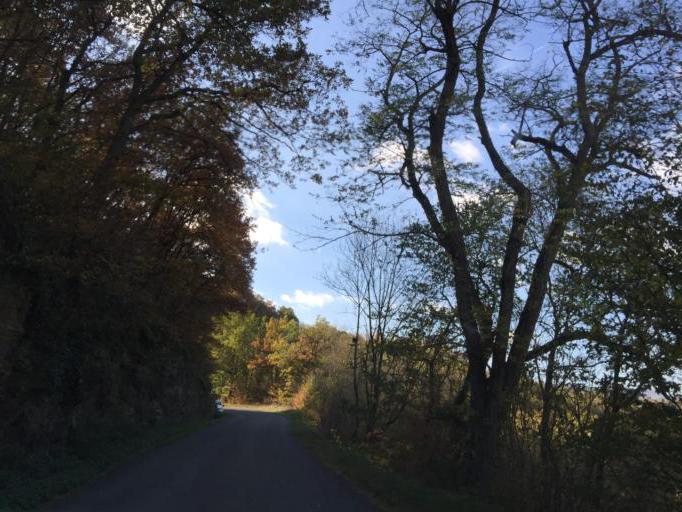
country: FR
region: Rhone-Alpes
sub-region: Departement de la Loire
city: Lorette
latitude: 45.5309
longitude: 4.5701
